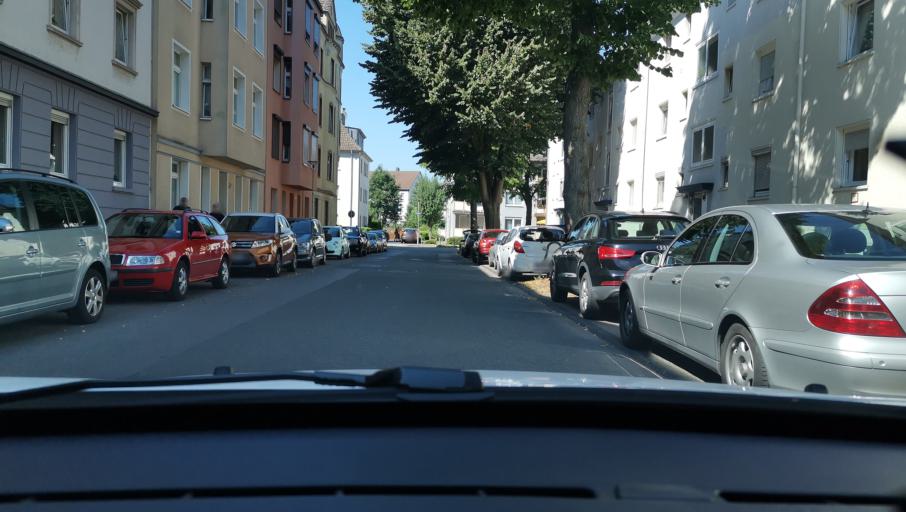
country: DE
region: North Rhine-Westphalia
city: Herdecke
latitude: 51.3823
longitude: 7.4533
